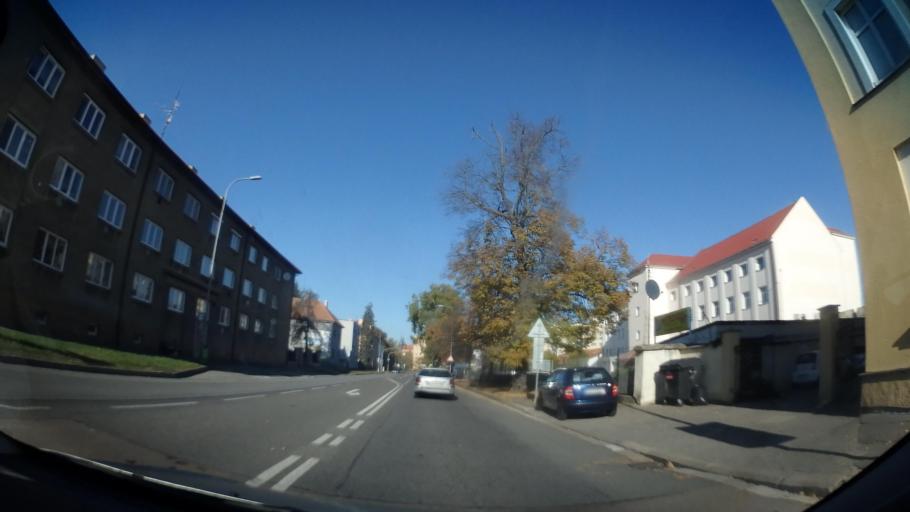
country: CZ
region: Pardubicky
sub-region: Okres Chrudim
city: Chrudim
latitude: 49.9425
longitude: 15.7949
